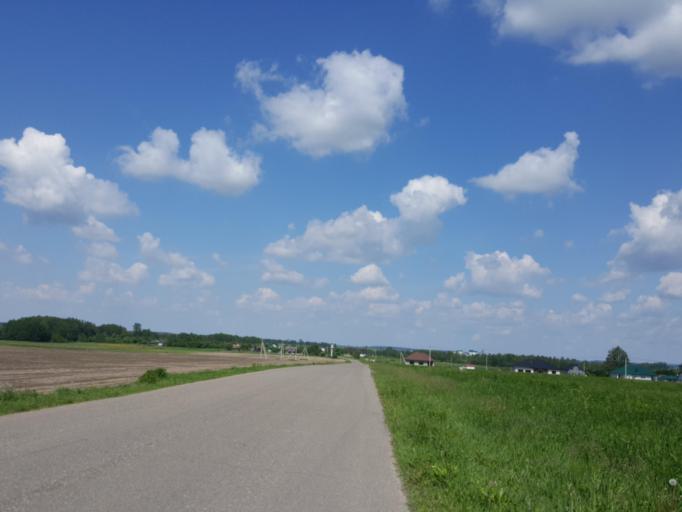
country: BY
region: Brest
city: Kamyanyets
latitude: 52.3827
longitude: 23.8089
